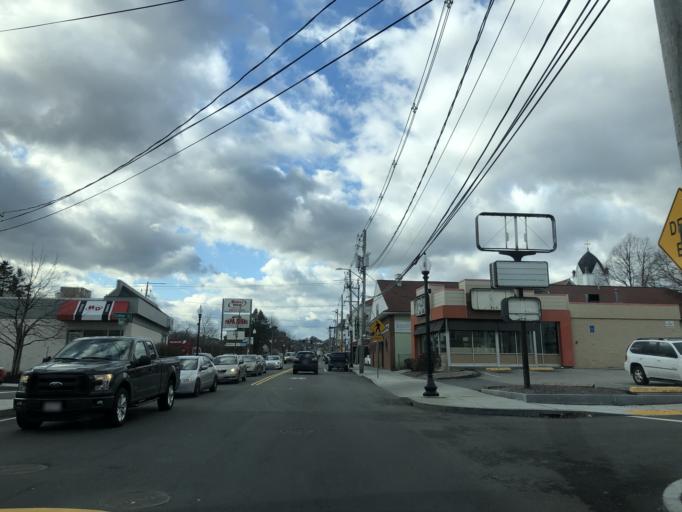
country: US
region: Massachusetts
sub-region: Bristol County
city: New Bedford
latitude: 41.6561
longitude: -70.9243
